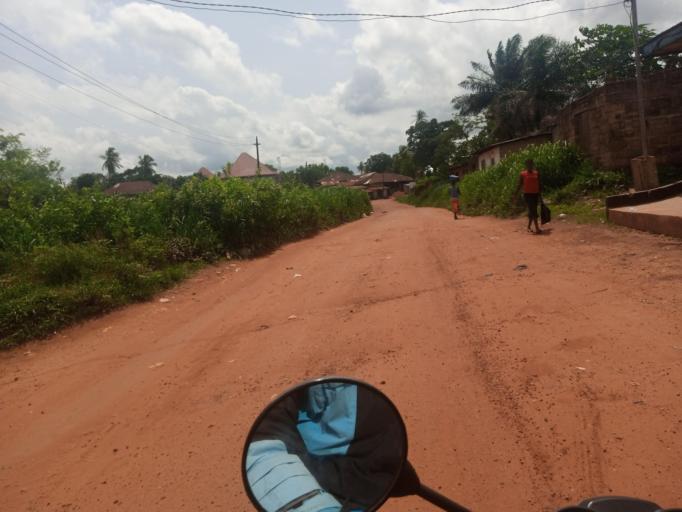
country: SL
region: Southern Province
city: Bo
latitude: 7.9652
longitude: -11.7437
